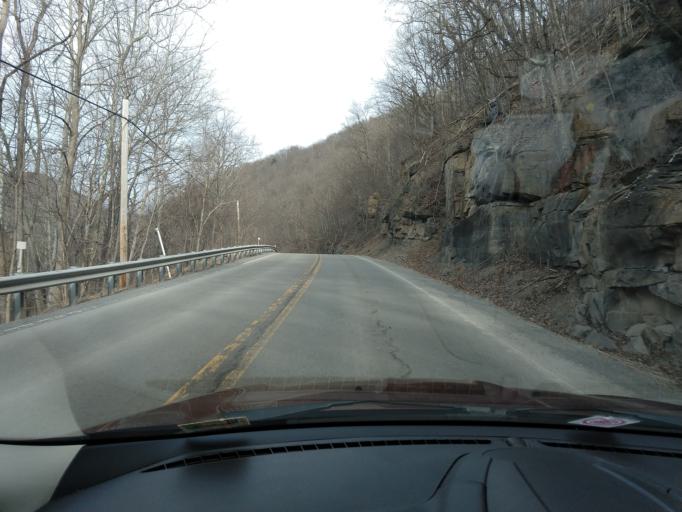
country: US
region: West Virginia
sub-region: Pendleton County
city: Franklin
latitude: 38.8613
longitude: -79.4442
